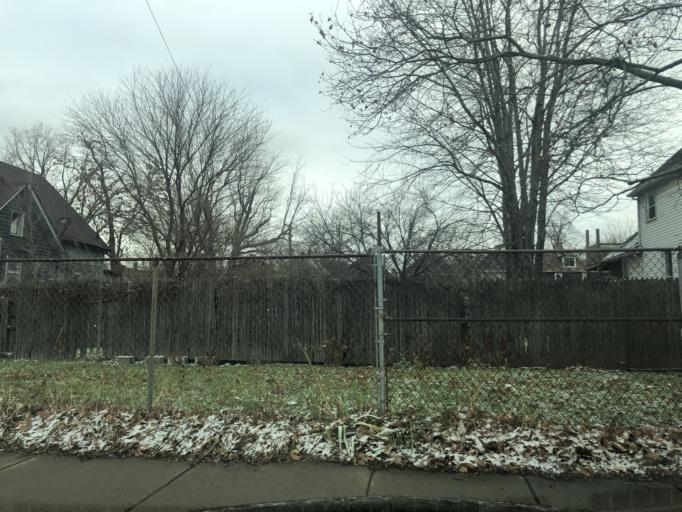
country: US
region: Michigan
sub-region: Wayne County
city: River Rouge
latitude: 42.3126
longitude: -83.0980
